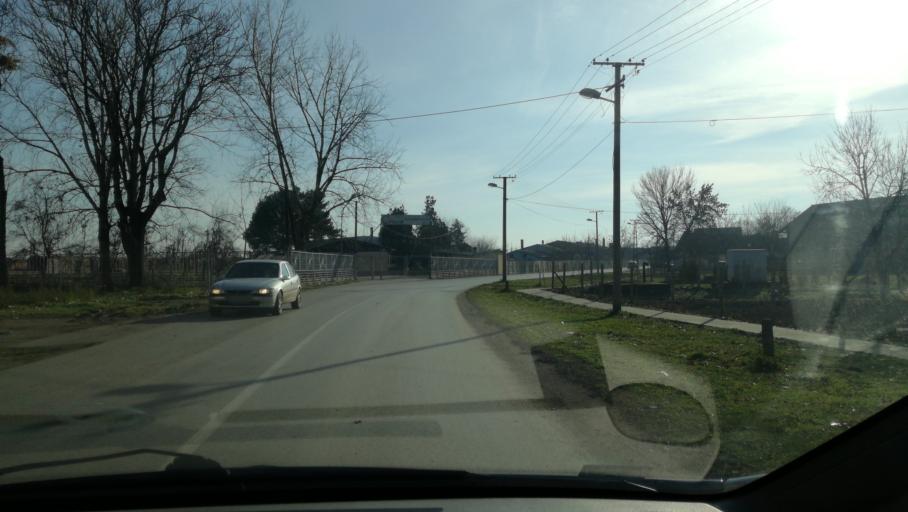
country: RS
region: Autonomna Pokrajina Vojvodina
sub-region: Severnobanatski Okrug
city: Kikinda
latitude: 45.8373
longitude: 20.4888
